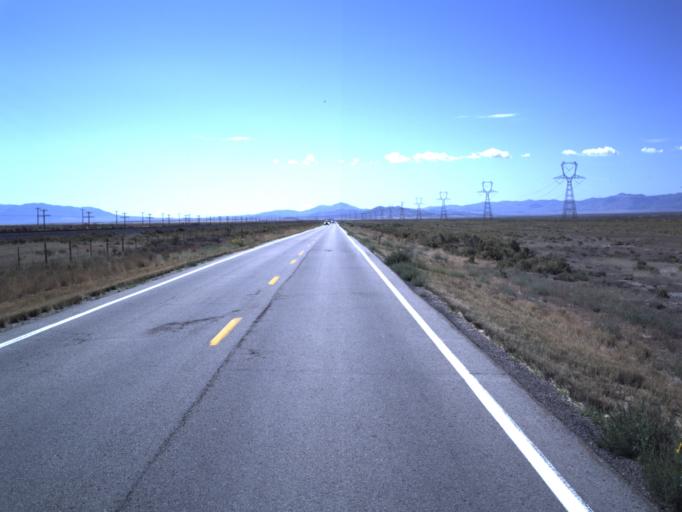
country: US
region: Utah
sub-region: Tooele County
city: Tooele
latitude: 40.3166
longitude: -112.4057
